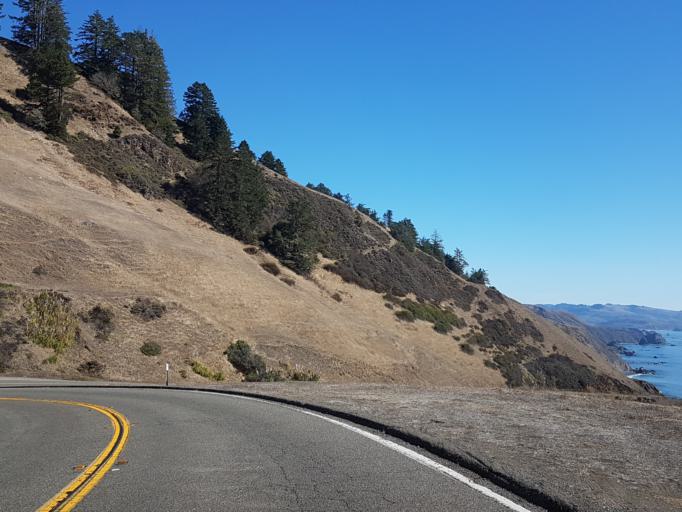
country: US
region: California
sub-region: Sonoma County
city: Monte Rio
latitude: 38.4953
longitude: -123.2004
